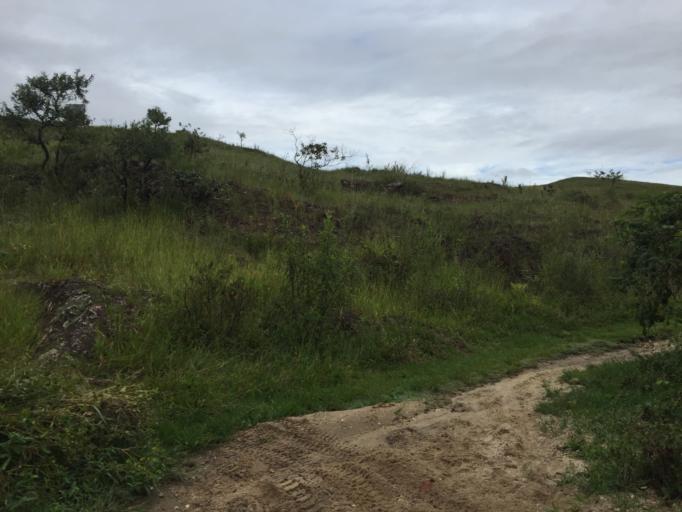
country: BR
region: Minas Gerais
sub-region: Sao Joao Del Rei
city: Sao Joao del Rei
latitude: -21.1288
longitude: -44.2691
